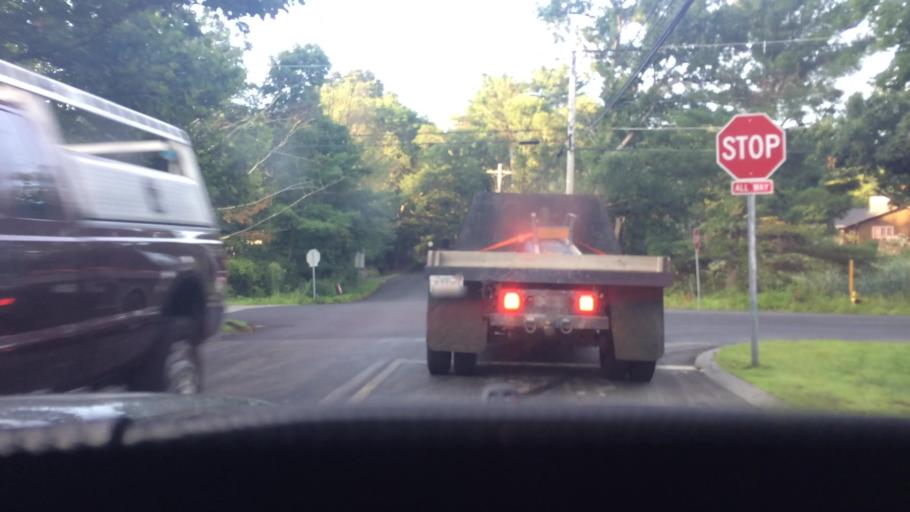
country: US
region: Massachusetts
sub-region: Middlesex County
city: North Reading
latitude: 42.6235
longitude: -71.0940
